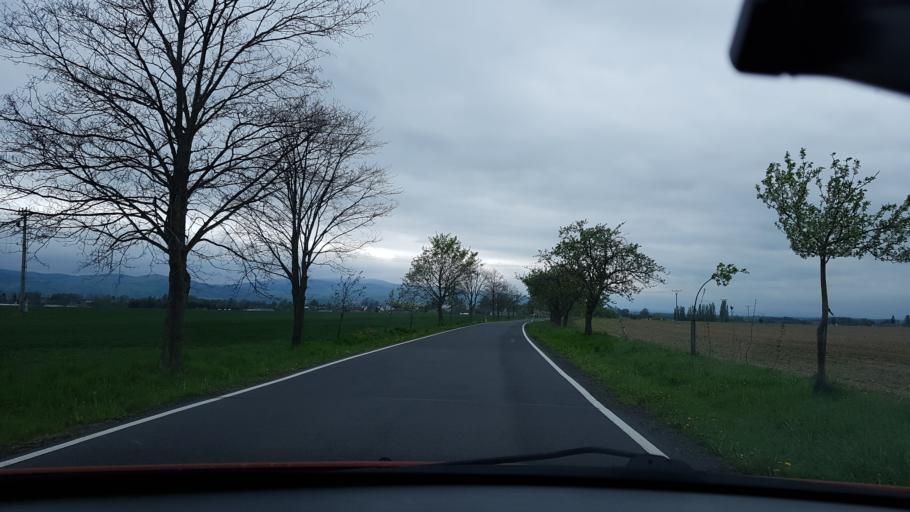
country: CZ
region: Olomoucky
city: Zulova
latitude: 50.3857
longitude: 17.0938
